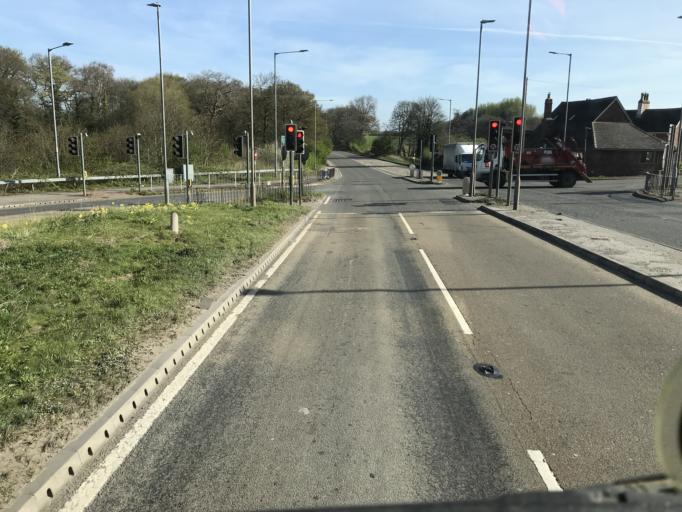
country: GB
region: England
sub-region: Cheshire East
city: Mere
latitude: 53.2808
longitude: -2.4369
